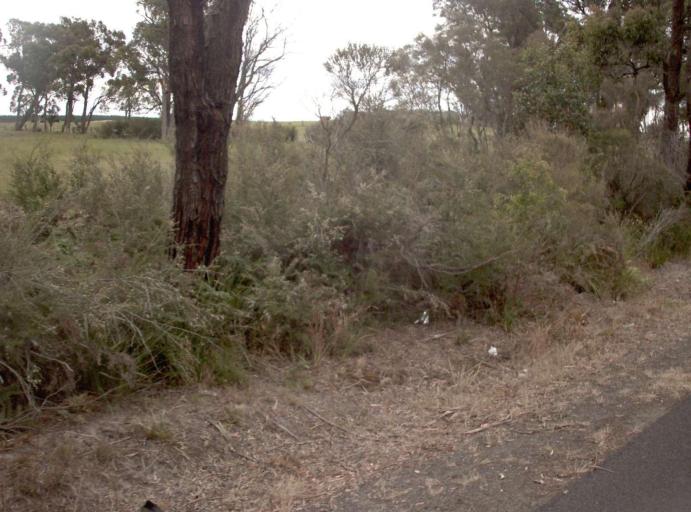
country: AU
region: Victoria
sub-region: Wellington
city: Sale
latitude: -38.2303
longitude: 147.0548
